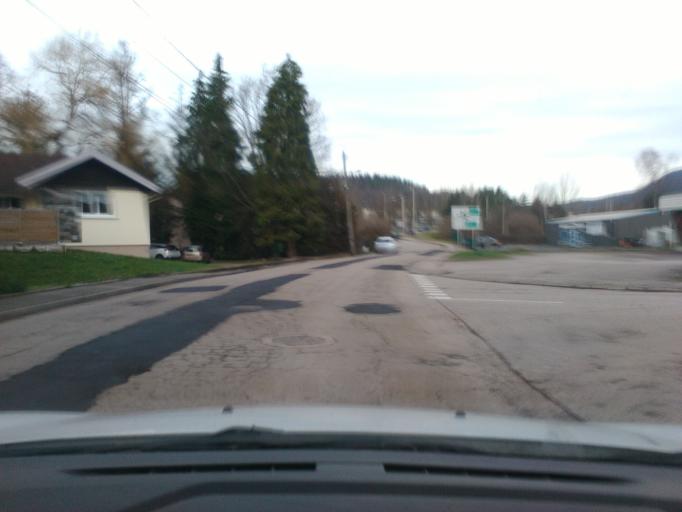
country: FR
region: Lorraine
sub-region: Departement des Vosges
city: Saint-Die-des-Vosges
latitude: 48.2912
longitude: 6.9283
